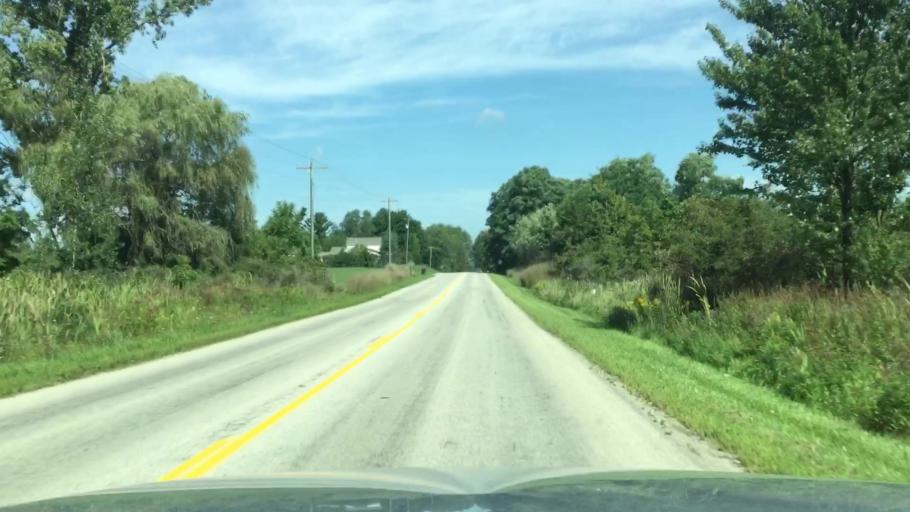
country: US
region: Michigan
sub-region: Lenawee County
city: Manitou Beach-Devils Lake
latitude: 42.0199
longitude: -84.2762
